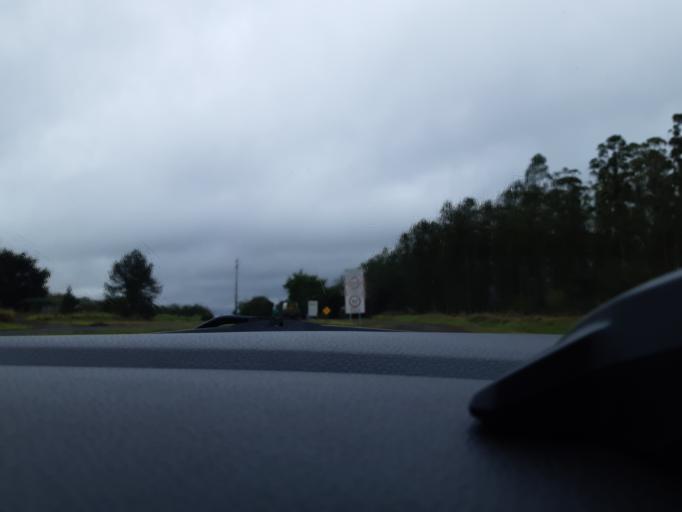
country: BR
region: Sao Paulo
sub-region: Ourinhos
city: Ourinhos
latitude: -22.9921
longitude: -49.9044
